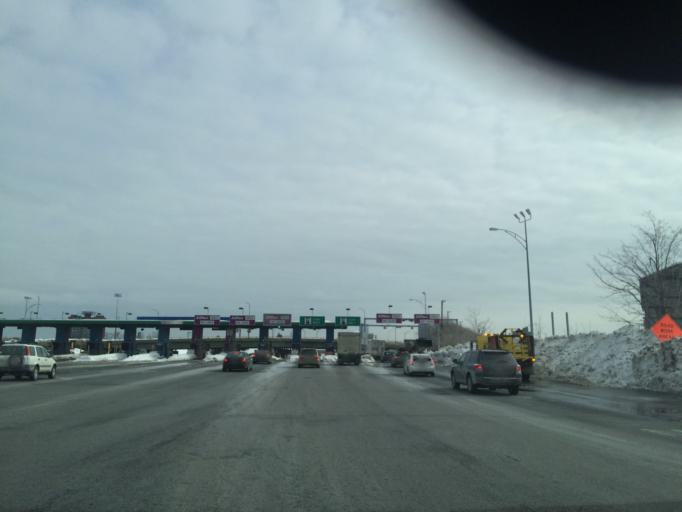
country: US
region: Massachusetts
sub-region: Middlesex County
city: Cambridge
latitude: 42.3573
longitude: -71.1229
